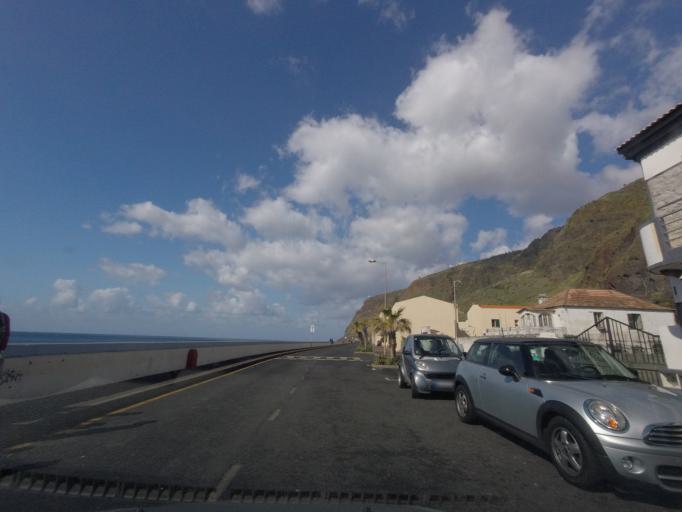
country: PT
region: Madeira
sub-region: Calheta
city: Faja da Ovelha
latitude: 32.7554
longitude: -17.2287
